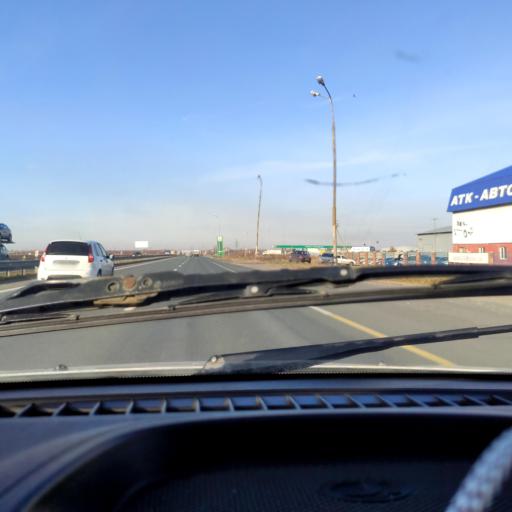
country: RU
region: Samara
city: Zhigulevsk
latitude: 53.5551
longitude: 49.5038
